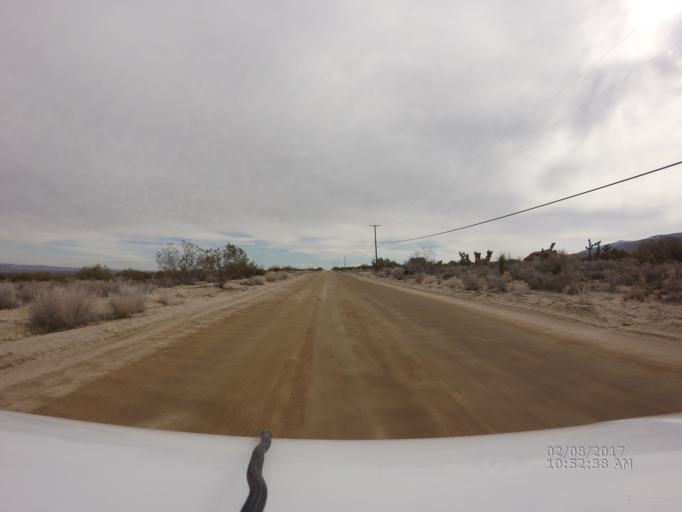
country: US
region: California
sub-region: San Bernardino County
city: Pinon Hills
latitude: 34.4695
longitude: -117.7408
